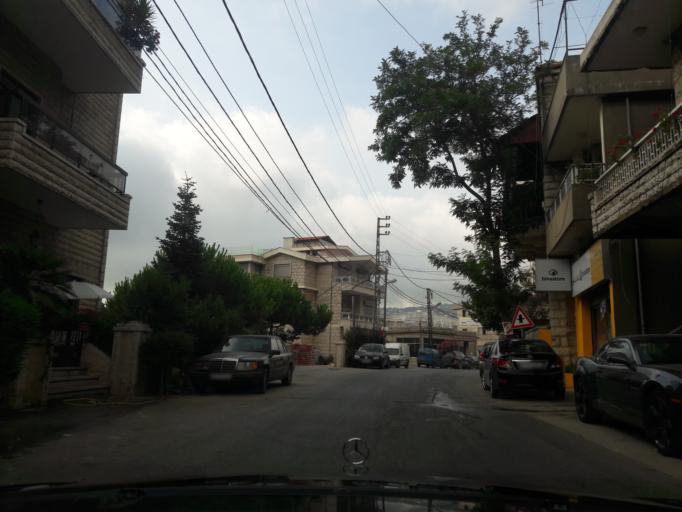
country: LB
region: Mont-Liban
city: Djounie
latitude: 33.9287
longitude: 35.7416
